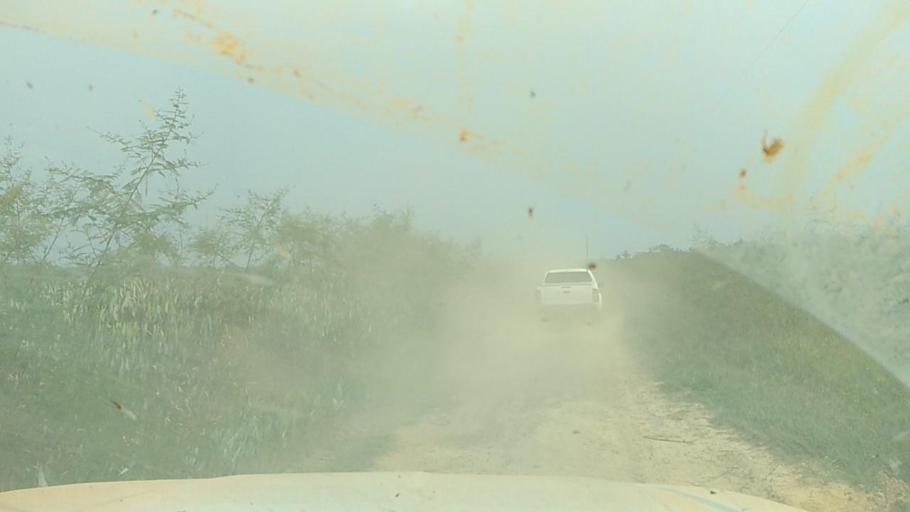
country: BR
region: Rondonia
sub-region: Porto Velho
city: Porto Velho
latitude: -8.9770
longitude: -64.3818
